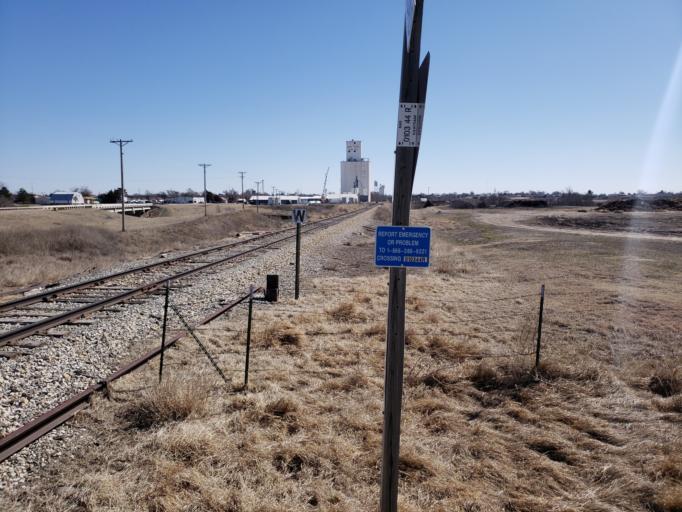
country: US
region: Kansas
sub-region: Ness County
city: Ness City
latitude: 38.4517
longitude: -99.9215
